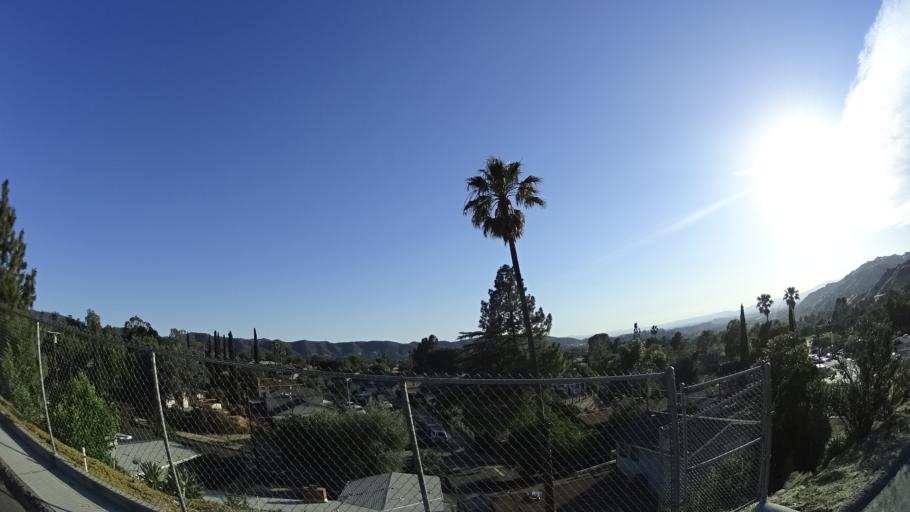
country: US
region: California
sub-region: Los Angeles County
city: La Crescenta-Montrose
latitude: 34.2700
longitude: -118.3002
